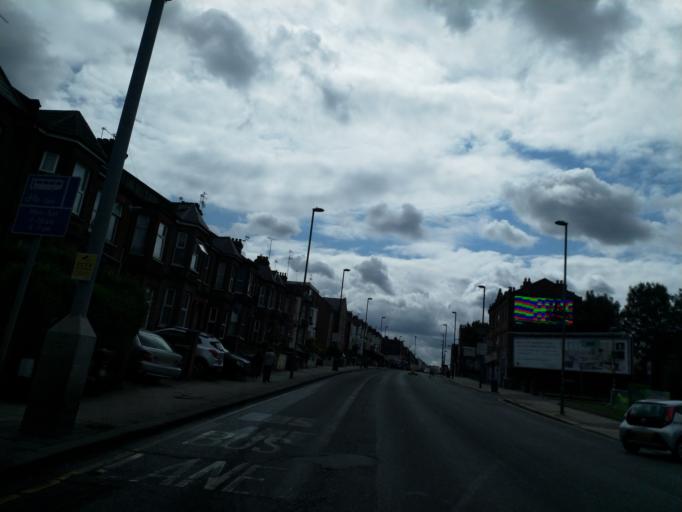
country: GB
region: England
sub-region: Greater London
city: Hendon
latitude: 51.5803
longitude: -0.2428
